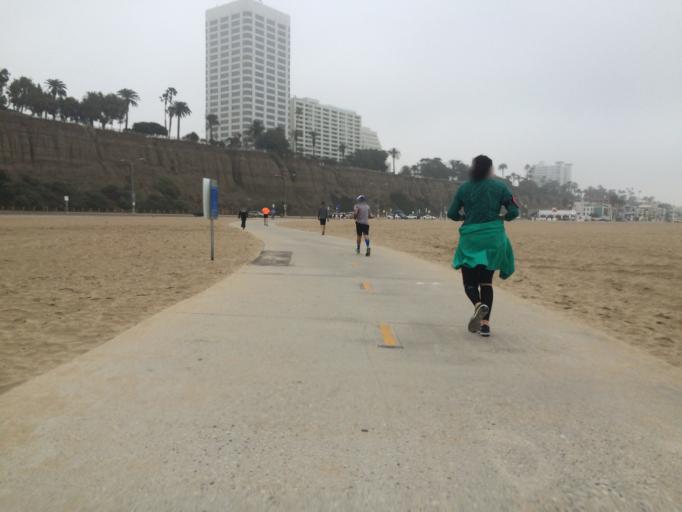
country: US
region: California
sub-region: Los Angeles County
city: Santa Monica
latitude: 34.0168
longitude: -118.5043
